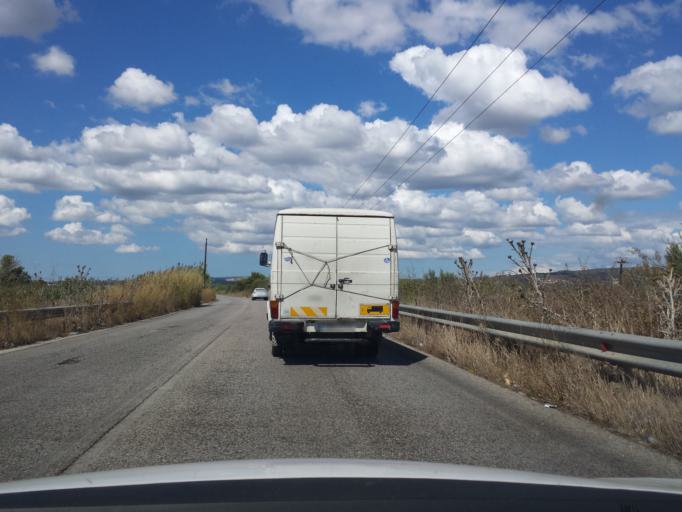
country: GR
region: West Greece
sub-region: Nomos Ileias
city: Epitalion
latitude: 37.6450
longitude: 21.4751
